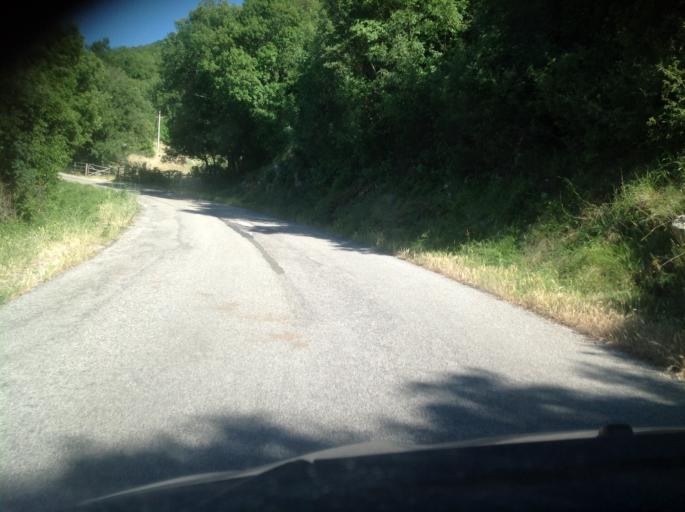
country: IT
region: Umbria
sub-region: Provincia di Terni
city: Stroncone
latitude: 42.4773
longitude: 12.6727
